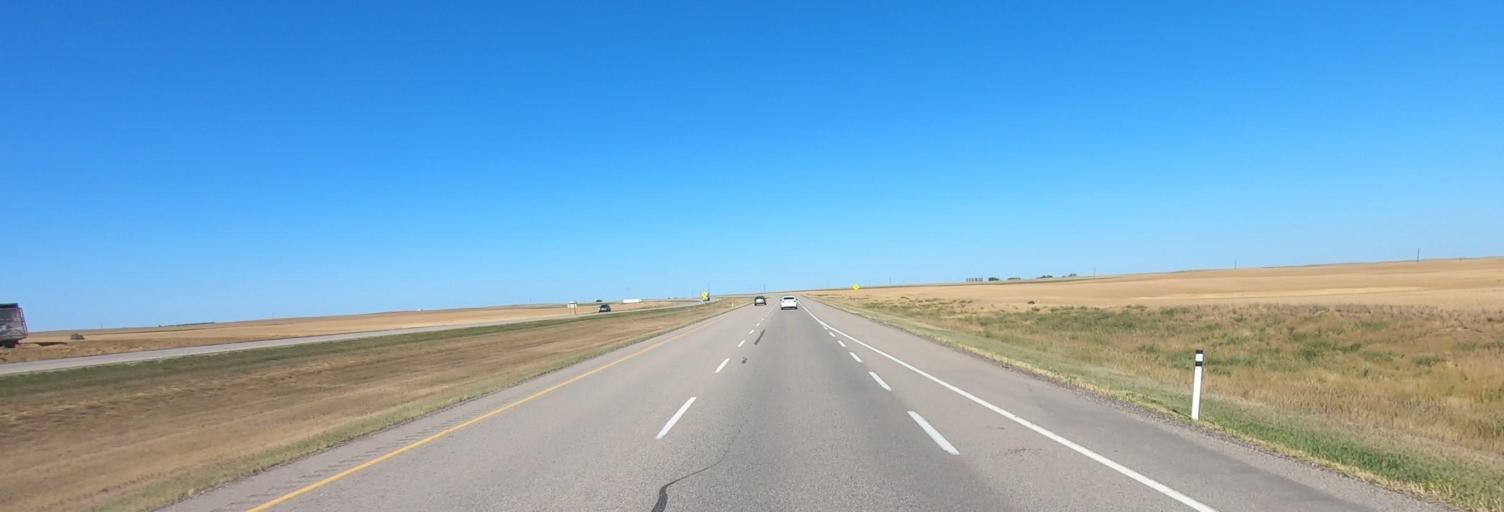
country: CA
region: Alberta
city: Bassano
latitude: 50.8284
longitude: -112.4648
